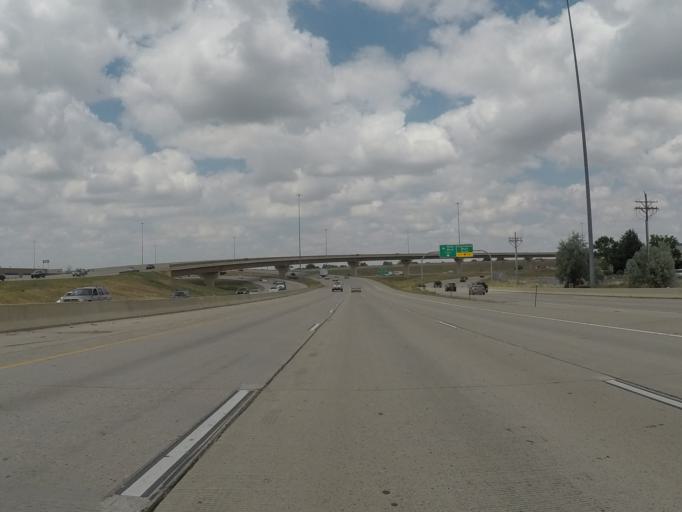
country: US
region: Colorado
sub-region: Adams County
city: Aurora
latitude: 39.7673
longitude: -104.8276
